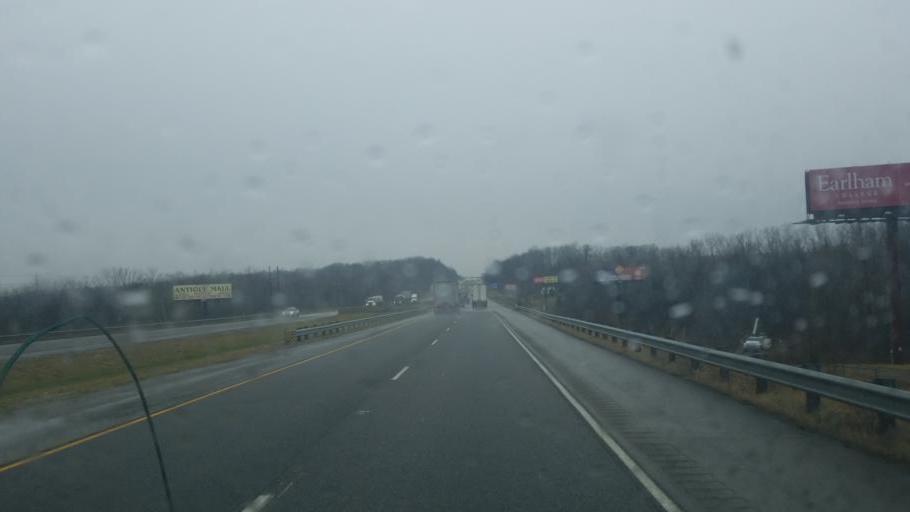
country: US
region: Ohio
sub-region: Preble County
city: New Paris
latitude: 39.8457
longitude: -84.8297
